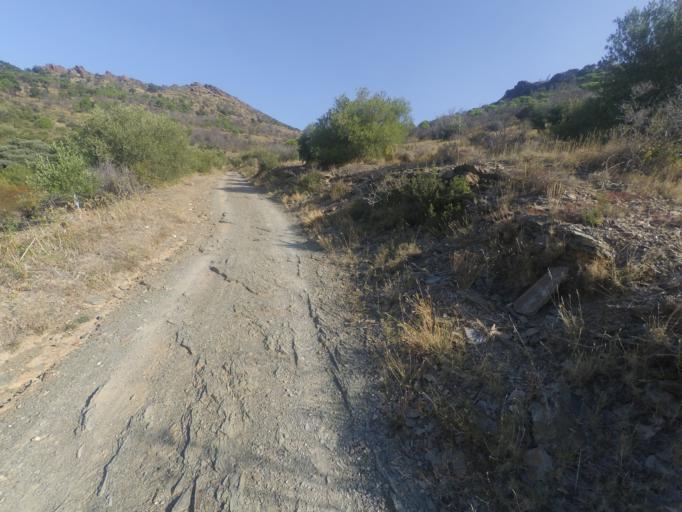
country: FR
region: Languedoc-Roussillon
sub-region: Departement des Pyrenees-Orientales
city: Corneilla-la-Riviere
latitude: 42.7278
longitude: 2.7122
